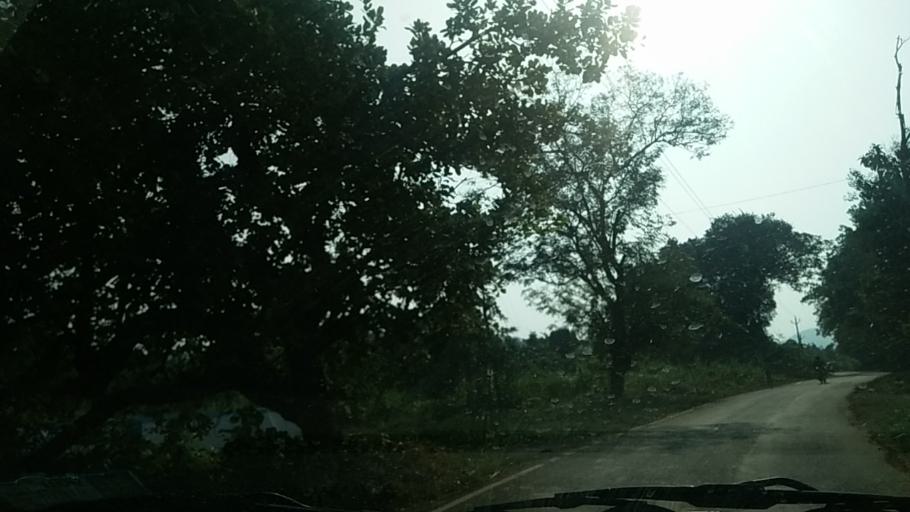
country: IN
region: Goa
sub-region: South Goa
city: Sanguem
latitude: 15.2272
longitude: 74.1872
